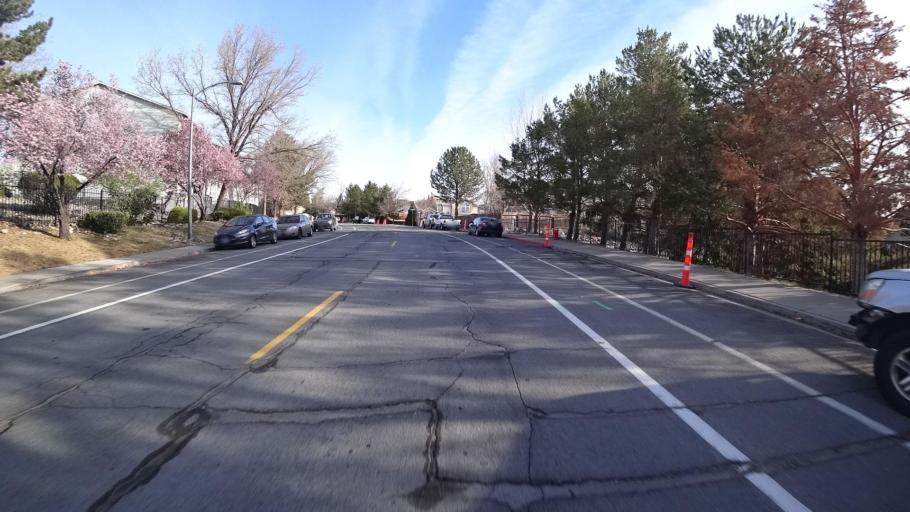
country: US
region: Nevada
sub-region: Washoe County
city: Reno
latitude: 39.5221
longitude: -119.8523
